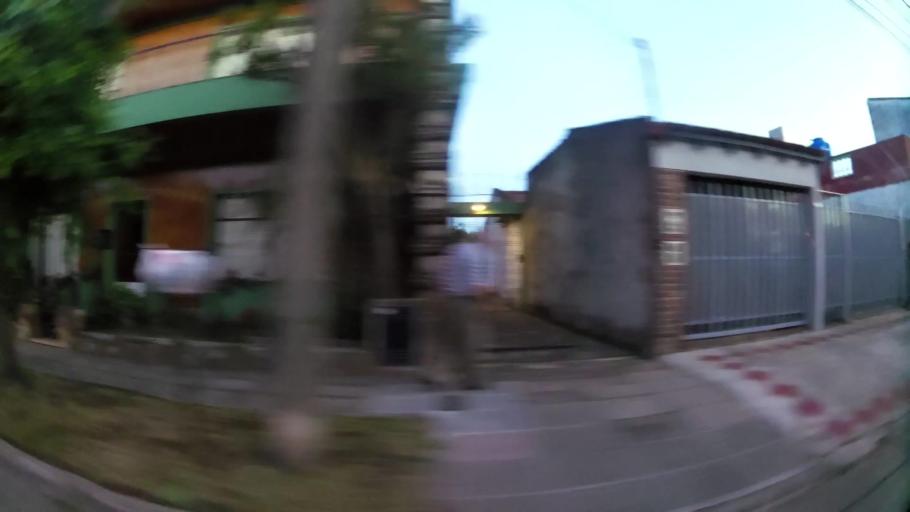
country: AR
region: Buenos Aires
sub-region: Partido de Moron
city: Moron
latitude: -34.6573
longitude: -58.6327
